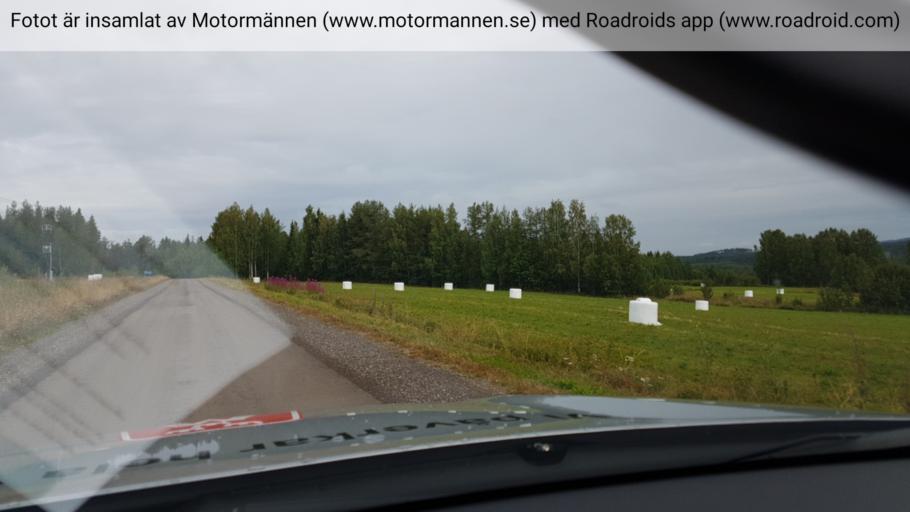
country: SE
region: Norrbotten
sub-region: Alvsbyns Kommun
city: AElvsbyn
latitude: 66.0275
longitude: 21.0079
